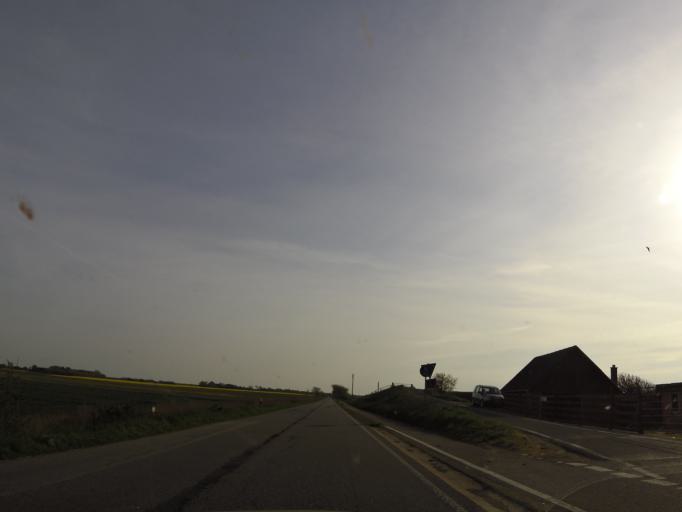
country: DE
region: Schleswig-Holstein
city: Galmsbull
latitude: 54.7411
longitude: 8.7252
